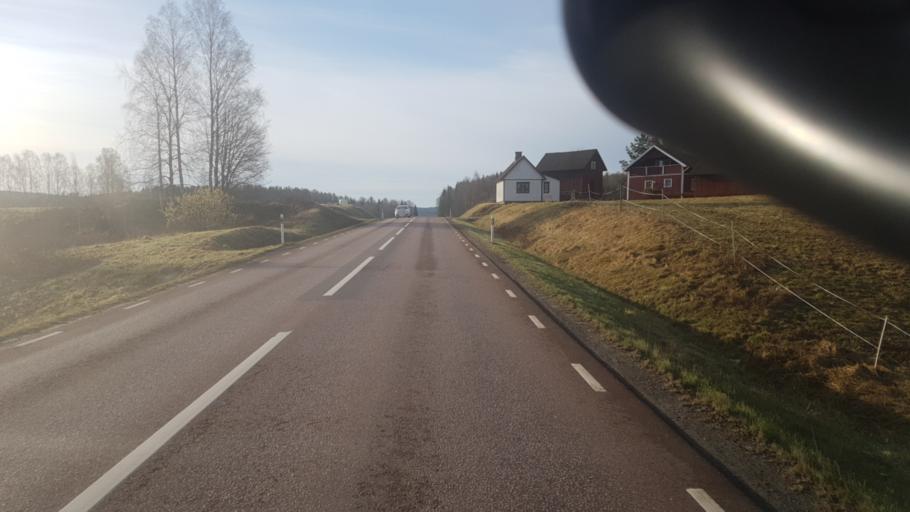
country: SE
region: Vaermland
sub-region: Eda Kommun
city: Charlottenberg
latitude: 59.8262
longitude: 12.3197
